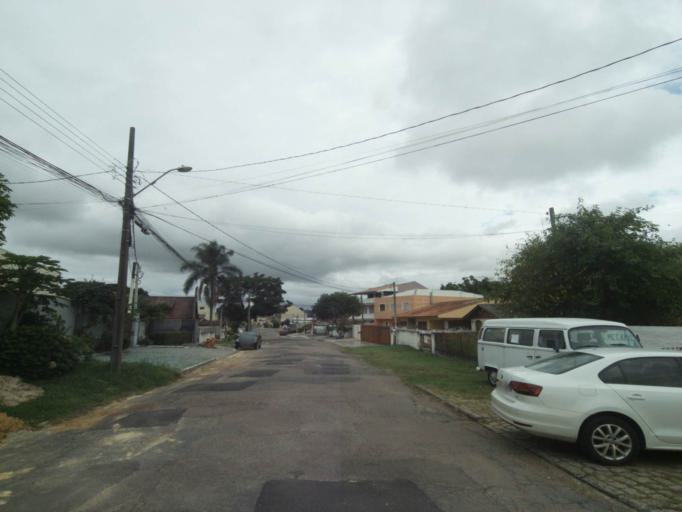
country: BR
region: Parana
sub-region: Curitiba
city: Curitiba
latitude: -25.4855
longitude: -49.2813
